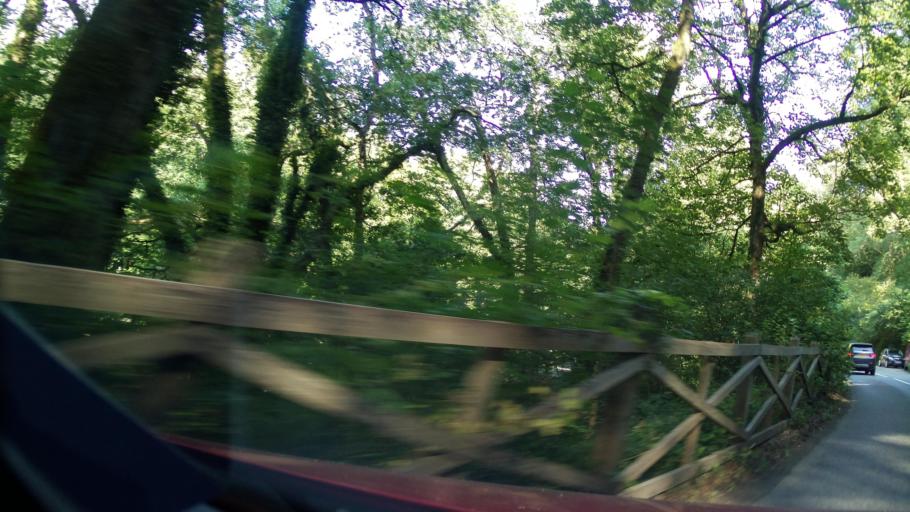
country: GB
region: England
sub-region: Devon
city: Ashburton
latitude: 50.5208
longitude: -3.7952
